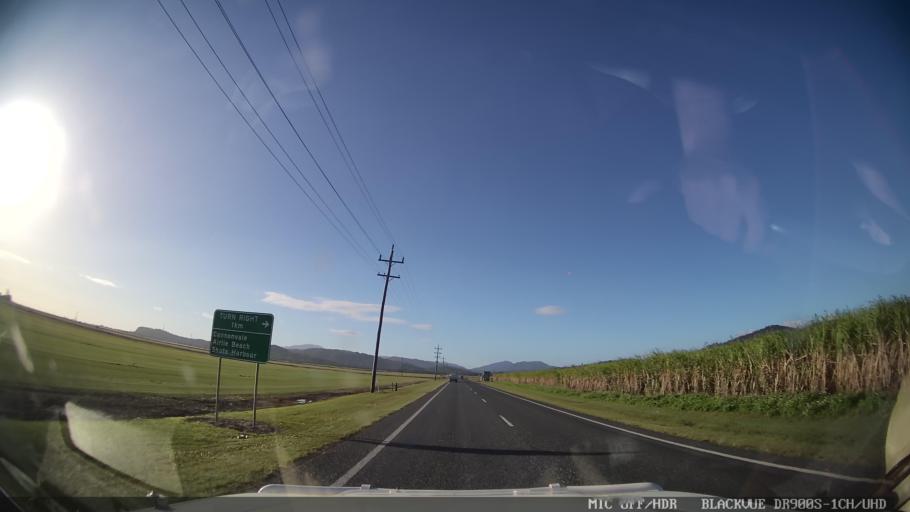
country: AU
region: Queensland
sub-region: Whitsunday
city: Proserpine
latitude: -20.3891
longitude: 148.5865
